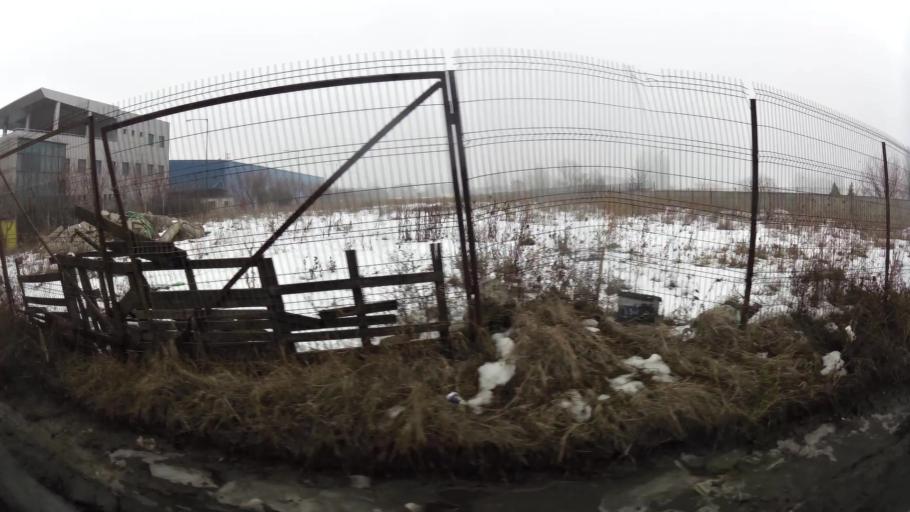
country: RO
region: Ilfov
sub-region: Comuna Chiajna
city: Chiajna
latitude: 44.4375
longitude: 25.9874
